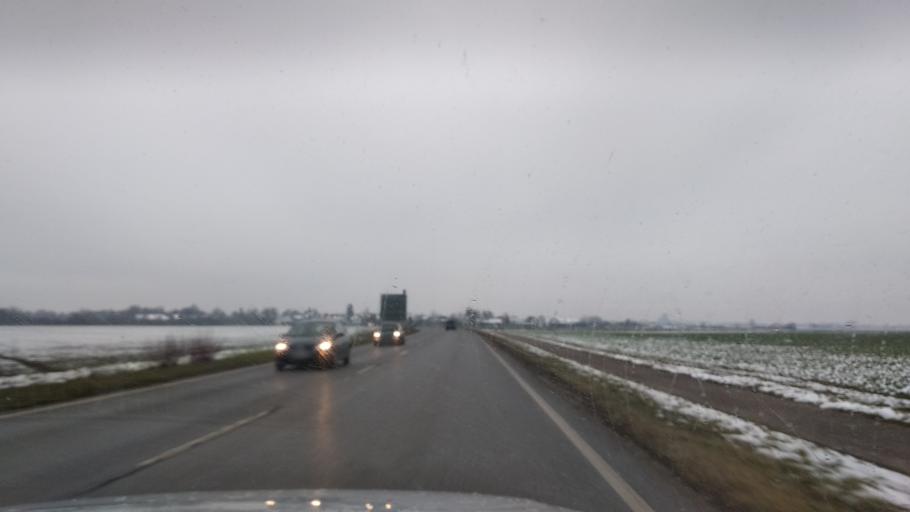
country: DE
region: Bavaria
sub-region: Upper Bavaria
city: Feldkirchen
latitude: 48.1374
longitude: 11.7361
